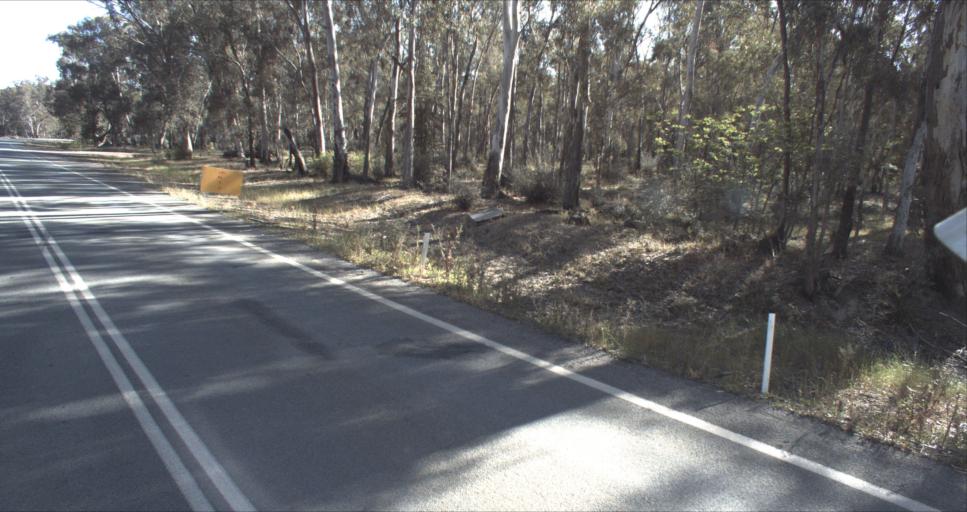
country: AU
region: New South Wales
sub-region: Leeton
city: Leeton
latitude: -34.6348
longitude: 146.3757
